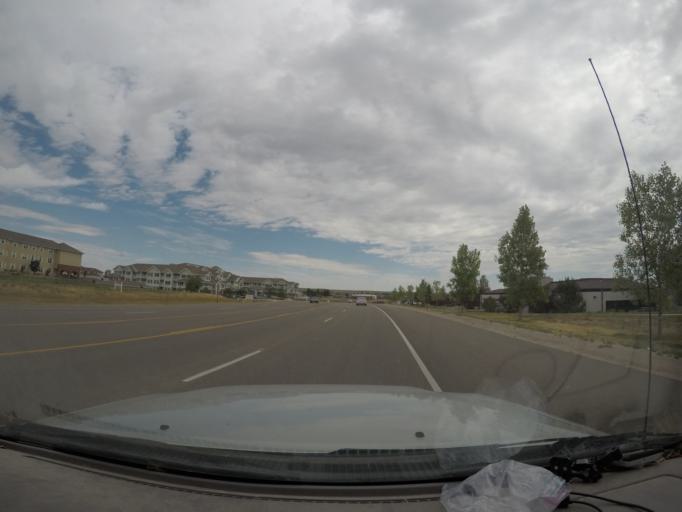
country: US
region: Wyoming
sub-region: Laramie County
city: Fox Farm-College
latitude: 41.1431
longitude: -104.7575
